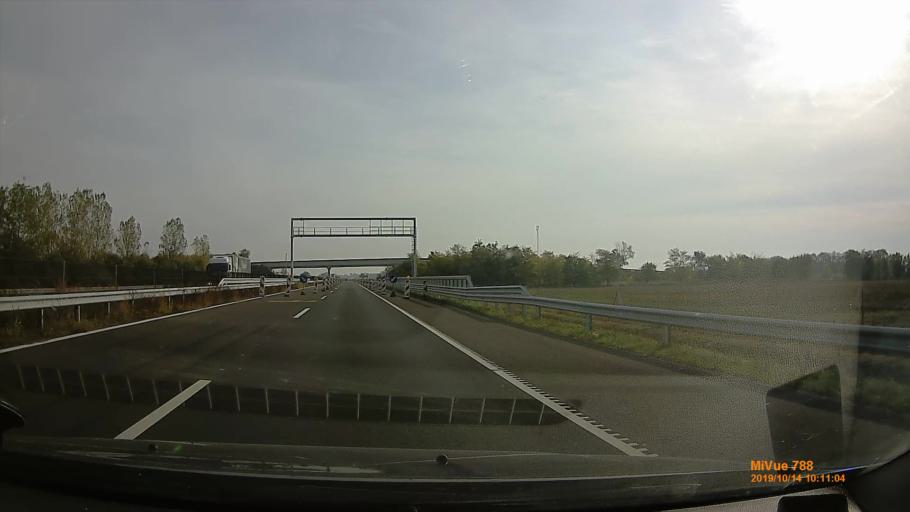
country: HU
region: Pest
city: Tortel
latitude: 47.1906
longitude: 19.8960
